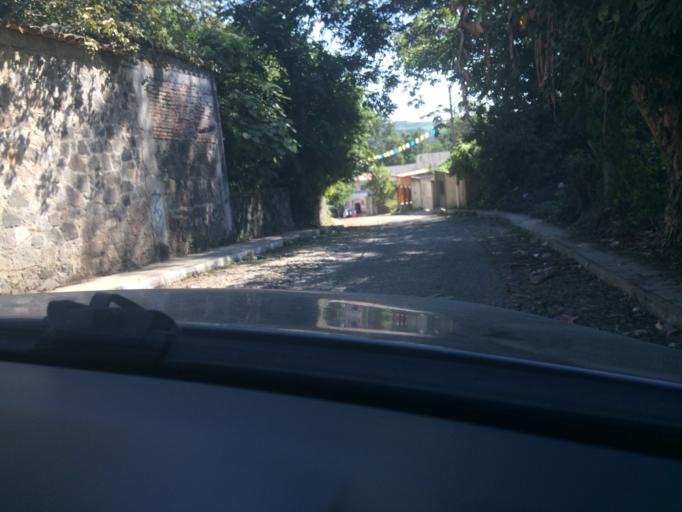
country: MX
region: Colima
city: Suchitlan
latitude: 19.3737
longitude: -103.7127
